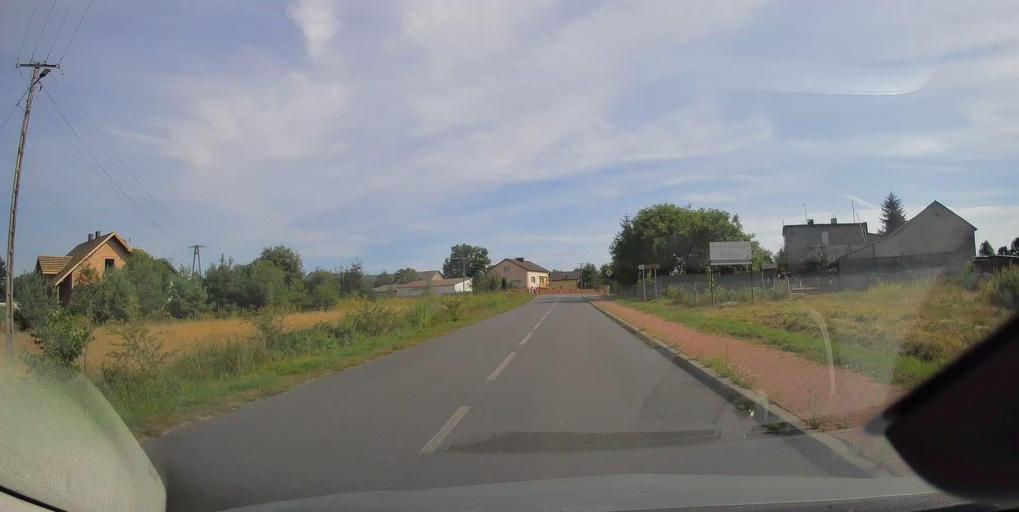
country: PL
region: Lodz Voivodeship
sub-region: Powiat opoczynski
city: Mniszkow
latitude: 51.4275
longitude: 20.0257
